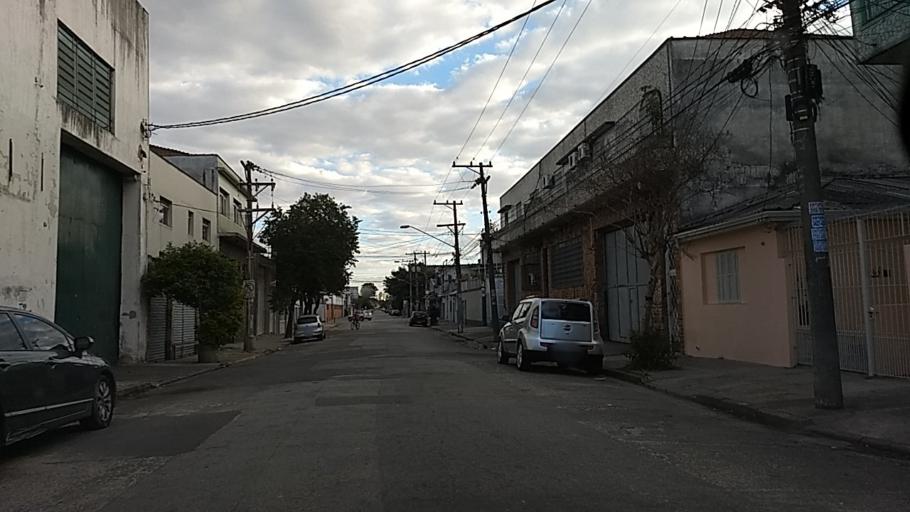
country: BR
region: Sao Paulo
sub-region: Sao Paulo
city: Sao Paulo
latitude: -23.5192
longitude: -46.5847
